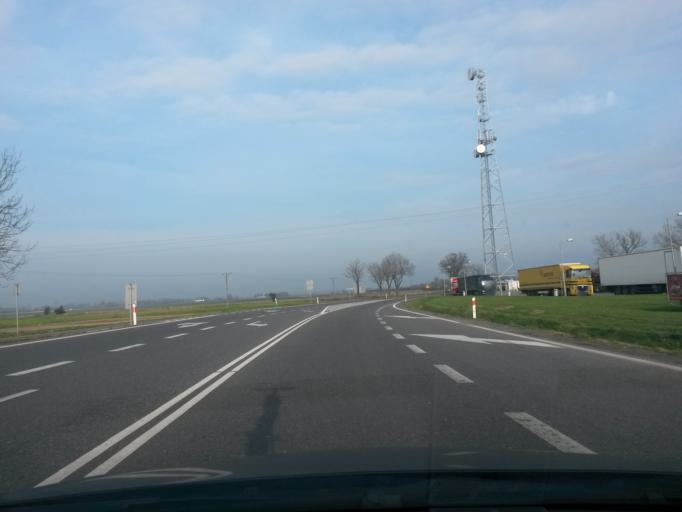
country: PL
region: Lower Silesian Voivodeship
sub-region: Powiat sredzki
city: Ciechow
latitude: 51.0373
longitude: 16.5834
